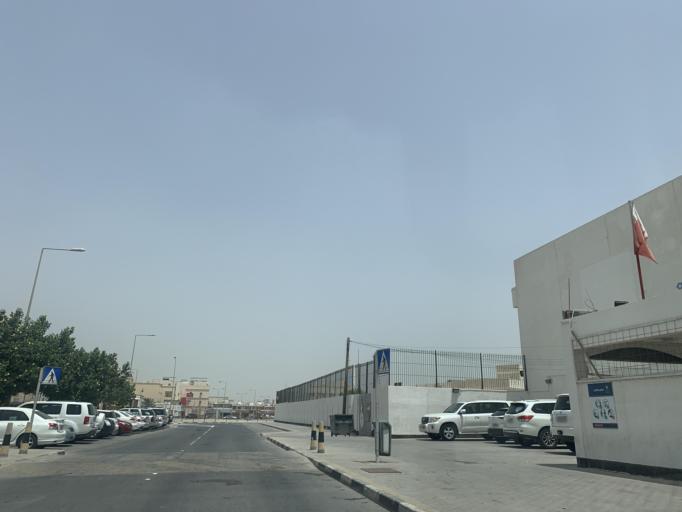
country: BH
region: Northern
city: Madinat `Isa
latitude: 26.1553
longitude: 50.5206
